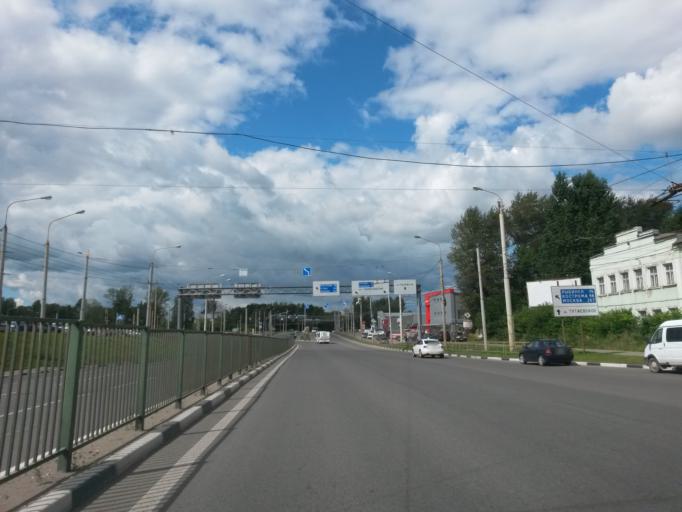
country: RU
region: Jaroslavl
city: Yaroslavl
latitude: 57.6709
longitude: 39.8392
